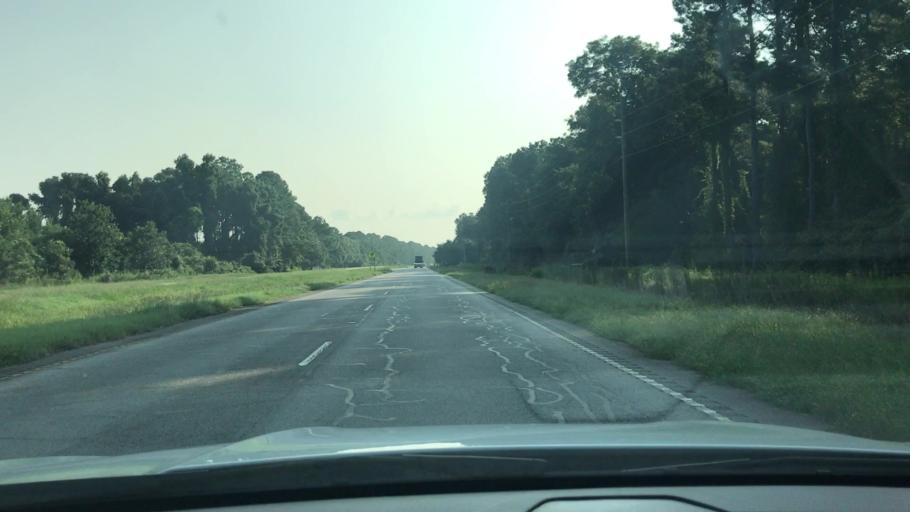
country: US
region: South Carolina
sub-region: Charleston County
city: Awendaw
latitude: 33.0585
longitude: -79.5418
